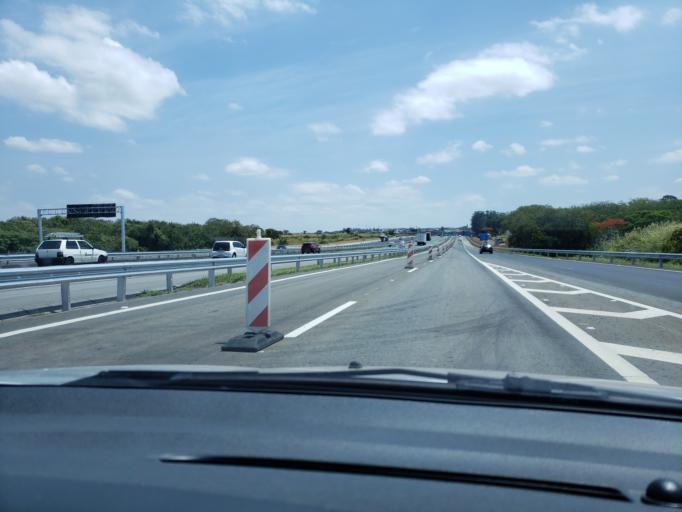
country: BR
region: Sao Paulo
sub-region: Campinas
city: Campinas
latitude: -22.8527
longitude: -47.1203
